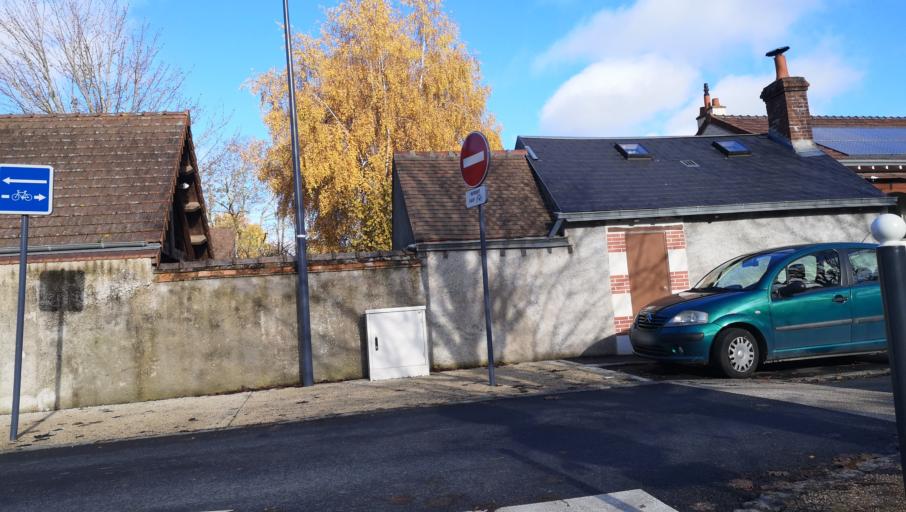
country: FR
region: Centre
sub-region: Departement du Loiret
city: Saint-Jean-le-Blanc
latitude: 47.9074
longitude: 1.9344
